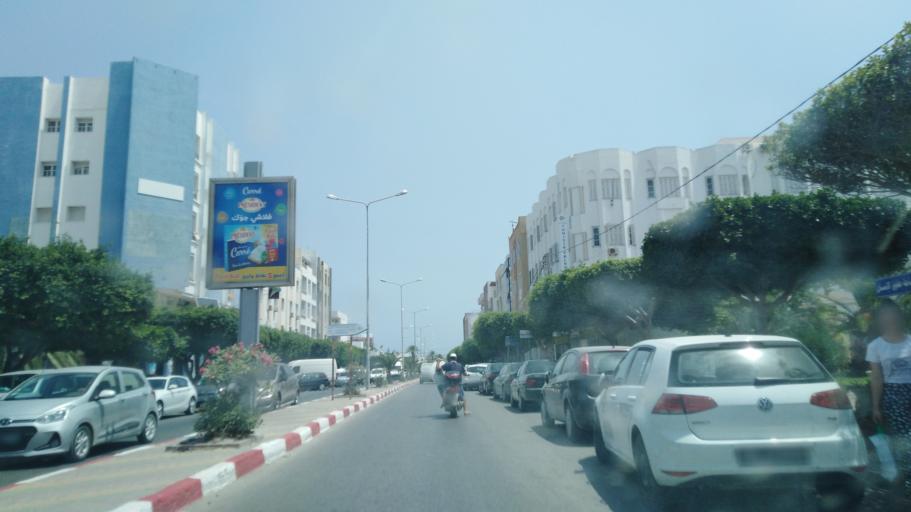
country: TN
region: Al Mahdiyah
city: Mahdia
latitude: 35.5074
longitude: 11.0522
